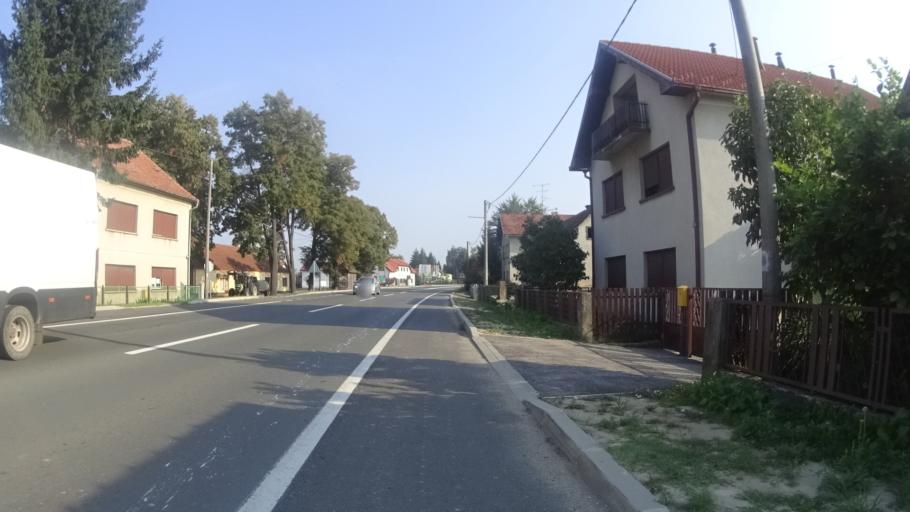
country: HR
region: Medimurska
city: Nedelisce
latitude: 46.3459
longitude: 16.3617
